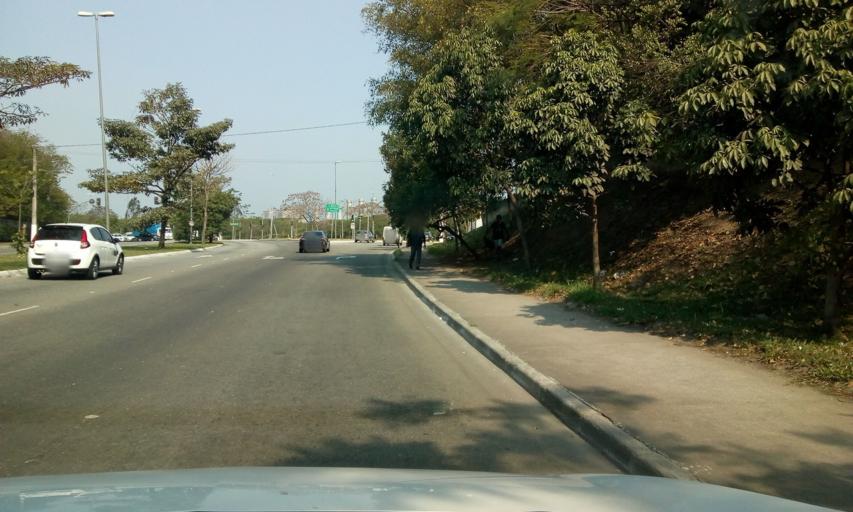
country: BR
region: Sao Paulo
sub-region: Diadema
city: Diadema
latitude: -23.6932
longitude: -46.6844
